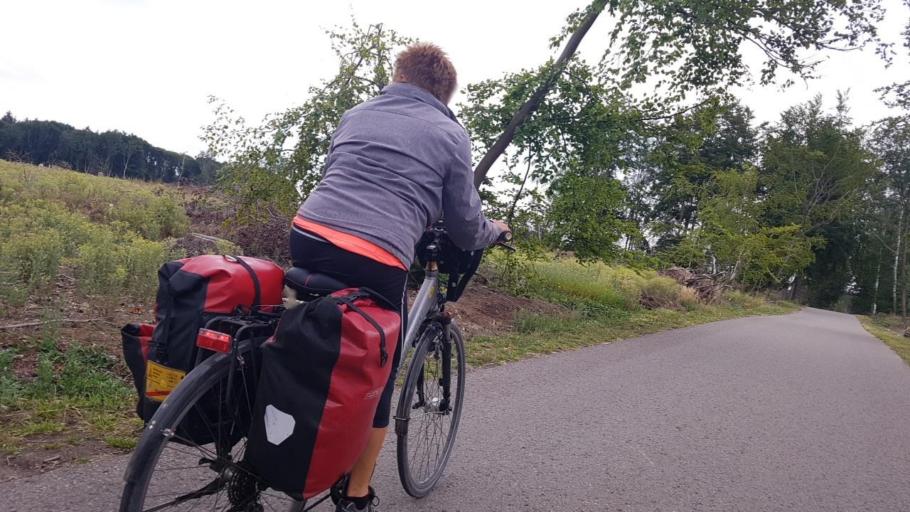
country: DE
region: North Rhine-Westphalia
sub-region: Regierungsbezirk Koln
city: Hurtgenwald
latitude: 50.7586
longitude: 6.3785
